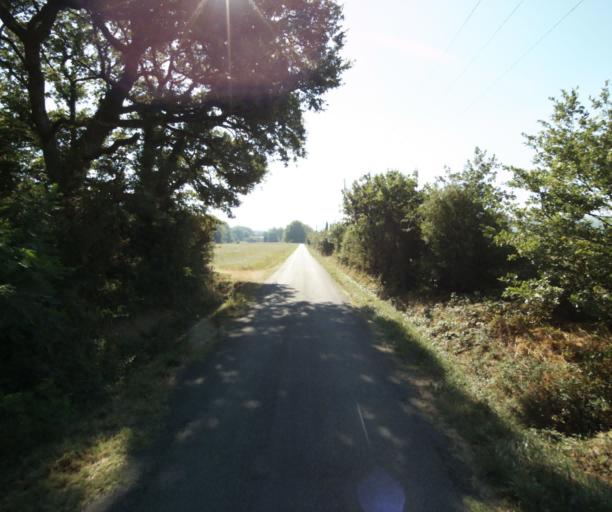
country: FR
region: Midi-Pyrenees
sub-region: Departement de la Haute-Garonne
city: Revel
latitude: 43.4653
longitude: 2.0146
